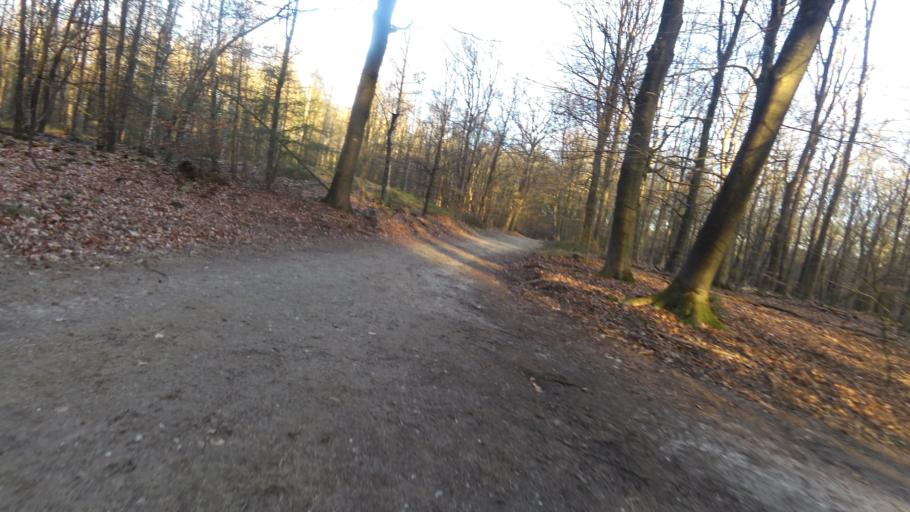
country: NL
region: Gelderland
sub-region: Gemeente Putten
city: Putten
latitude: 52.2469
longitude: 5.6504
